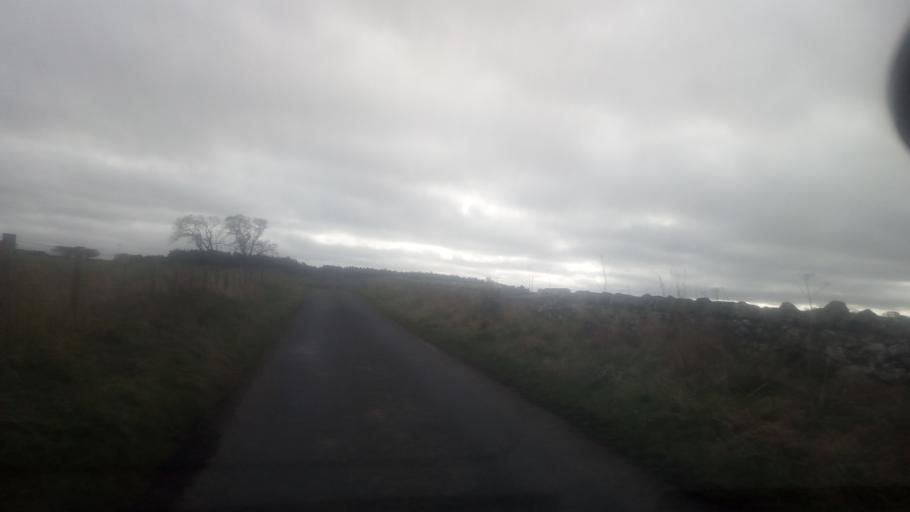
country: GB
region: Scotland
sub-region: The Scottish Borders
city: Kelso
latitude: 55.5686
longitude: -2.5125
